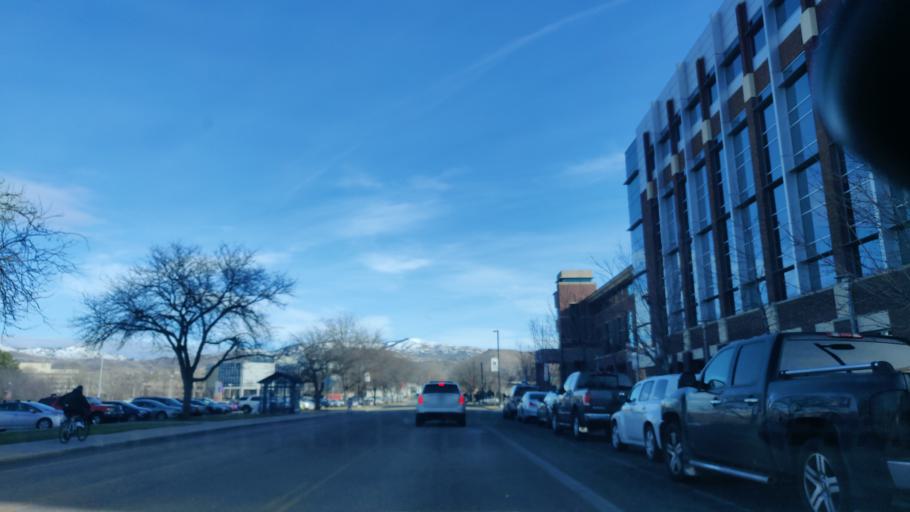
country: US
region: Idaho
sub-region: Ada County
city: Boise
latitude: 43.6010
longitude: -116.1971
